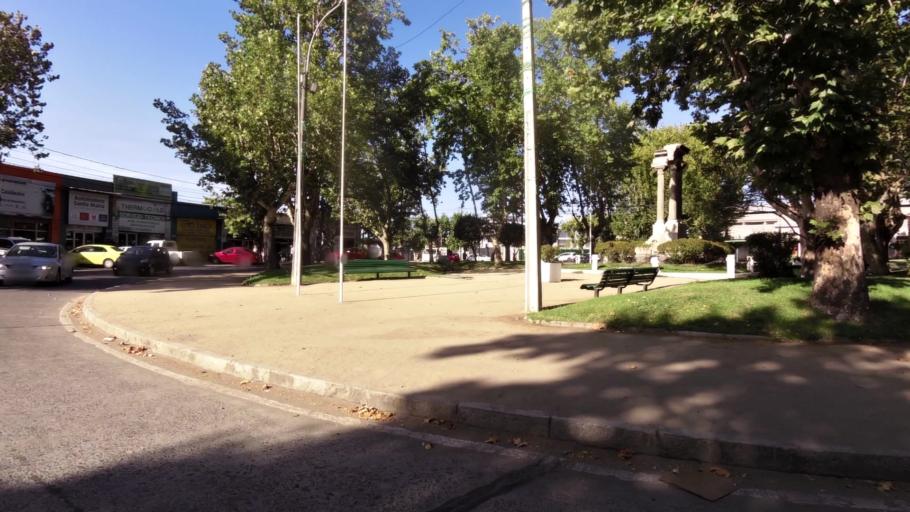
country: CL
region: Maule
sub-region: Provincia de Talca
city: Talca
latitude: -35.4295
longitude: -71.6510
